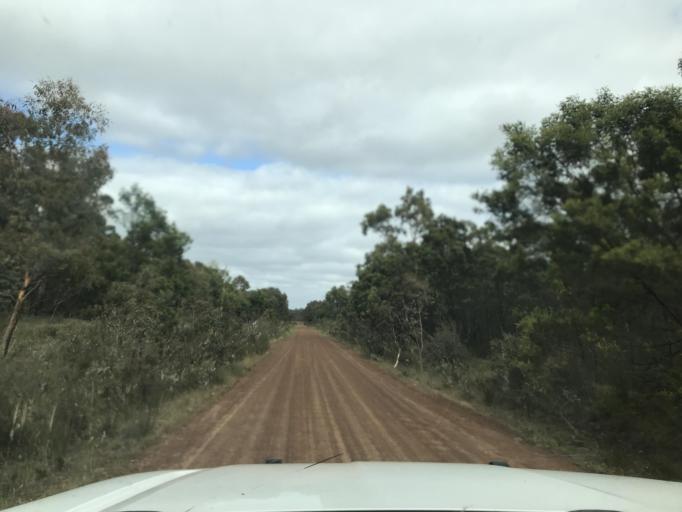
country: AU
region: South Australia
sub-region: Wattle Range
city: Penola
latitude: -37.3344
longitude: 141.4199
